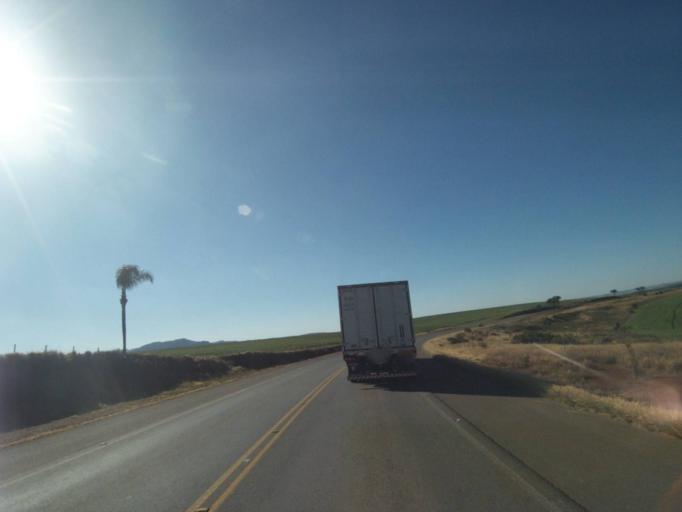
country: BR
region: Parana
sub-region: Tibagi
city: Tibagi
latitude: -24.6359
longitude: -50.4609
